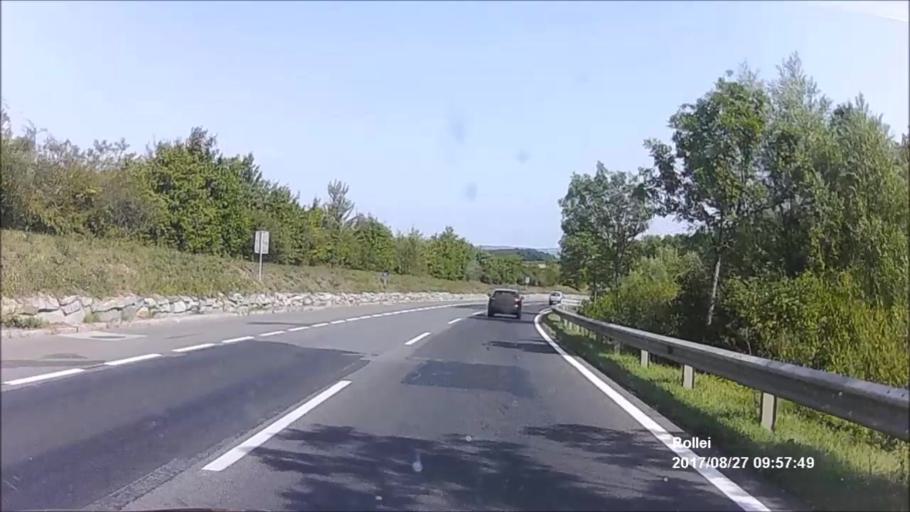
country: AT
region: Burgenland
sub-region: Eisenstadt-Umgebung
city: Klingenbach
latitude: 47.7487
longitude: 16.5456
